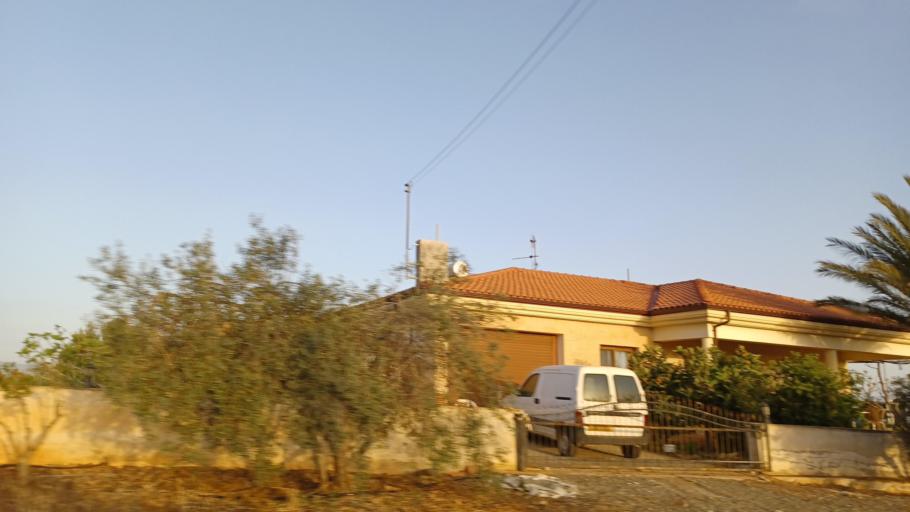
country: CY
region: Lefkosia
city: Astromeritis
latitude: 35.0892
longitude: 33.0145
